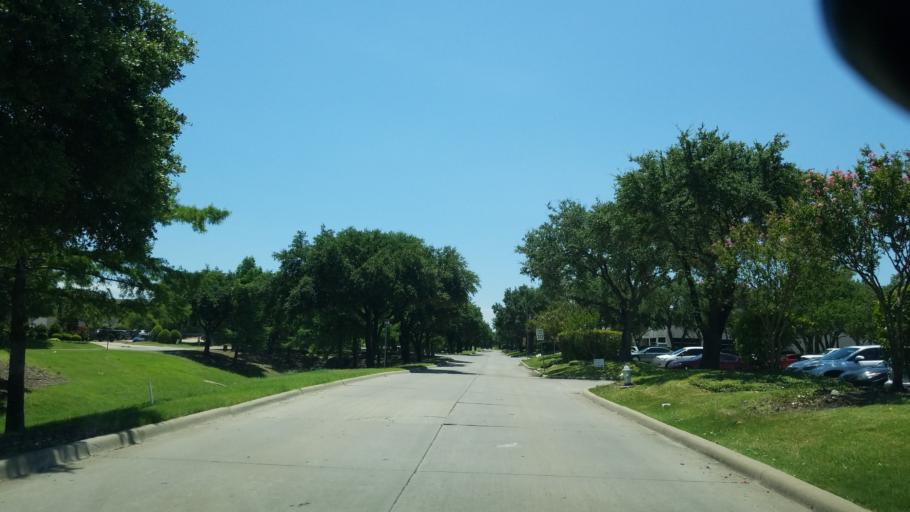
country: US
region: Texas
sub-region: Dallas County
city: Farmers Branch
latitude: 32.9305
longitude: -96.9153
